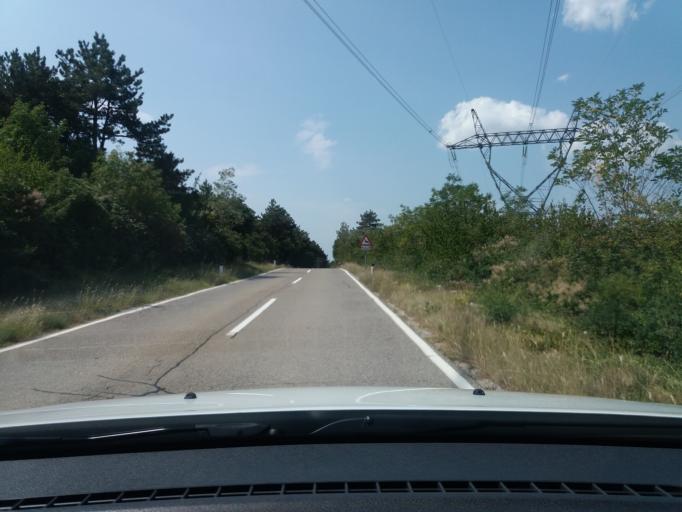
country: SI
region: Miren-Kostanjevica
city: Miren
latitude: 45.8729
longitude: 13.5919
